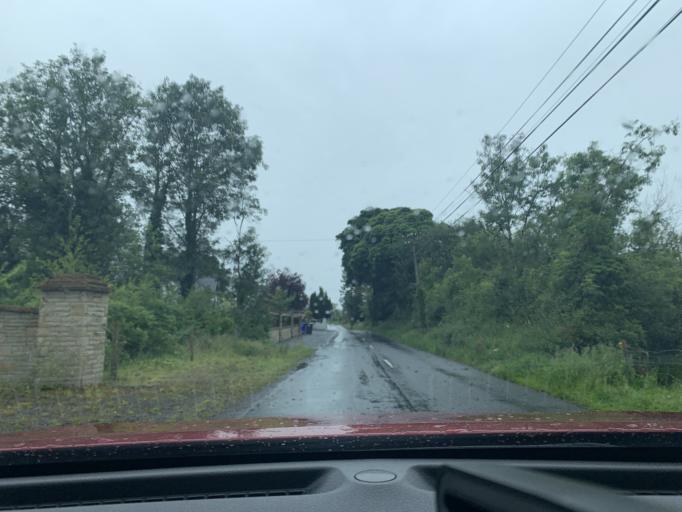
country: GB
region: Northern Ireland
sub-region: Fermanagh District
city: Enniskillen
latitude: 54.2876
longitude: -7.8982
